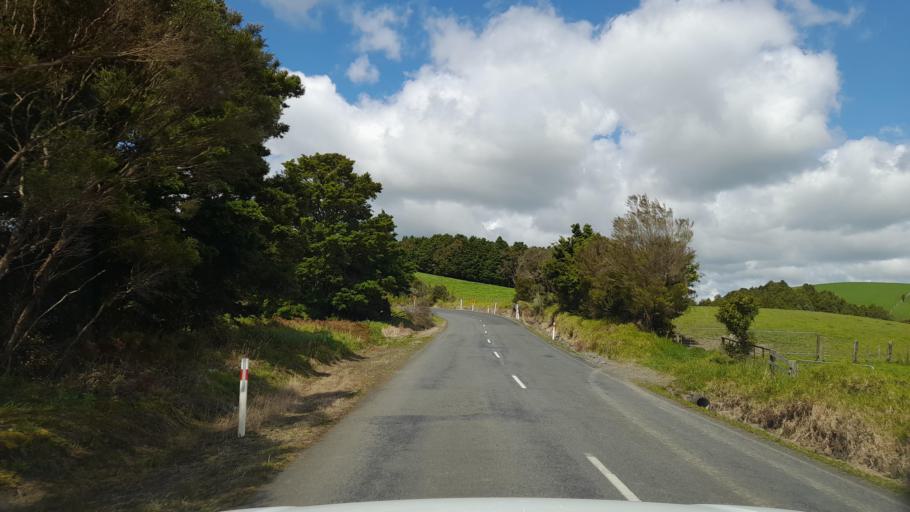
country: NZ
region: Northland
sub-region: Whangarei
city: Maungatapere
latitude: -35.6392
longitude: 174.0621
